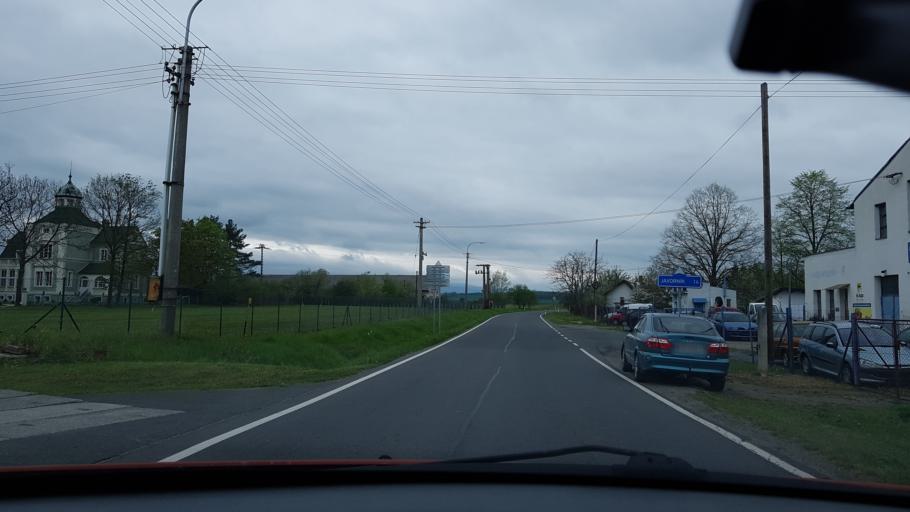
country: CZ
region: Olomoucky
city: Vidnava
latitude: 50.3739
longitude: 17.1809
